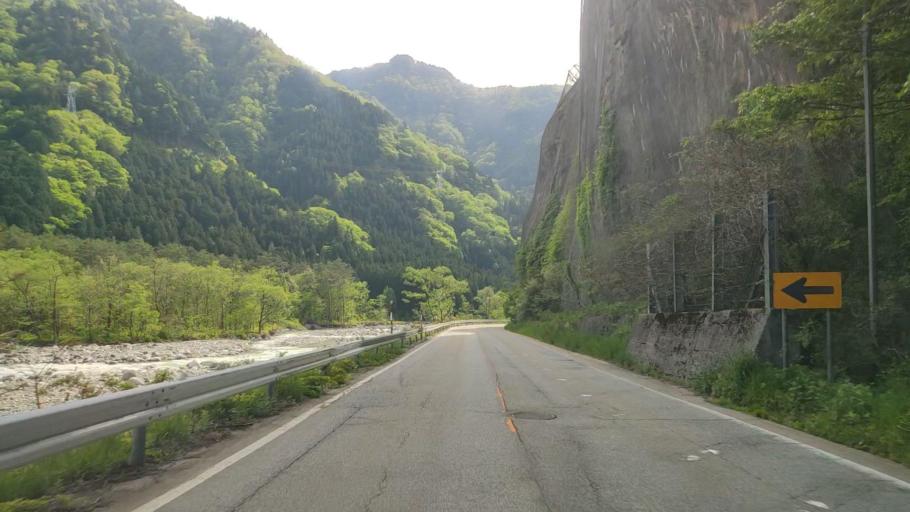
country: JP
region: Gifu
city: Takayama
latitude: 36.2499
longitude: 137.4897
